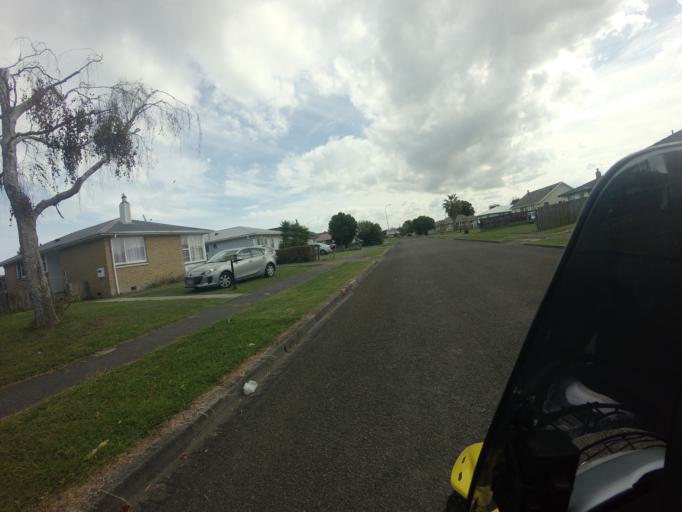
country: NZ
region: Gisborne
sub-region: Gisborne District
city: Gisborne
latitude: -38.6732
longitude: 178.0545
